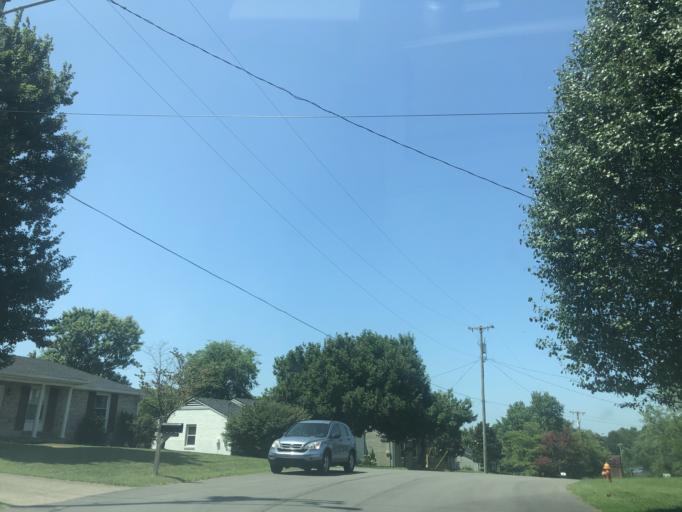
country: US
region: Tennessee
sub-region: Davidson County
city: Nashville
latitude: 36.1870
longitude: -86.7082
